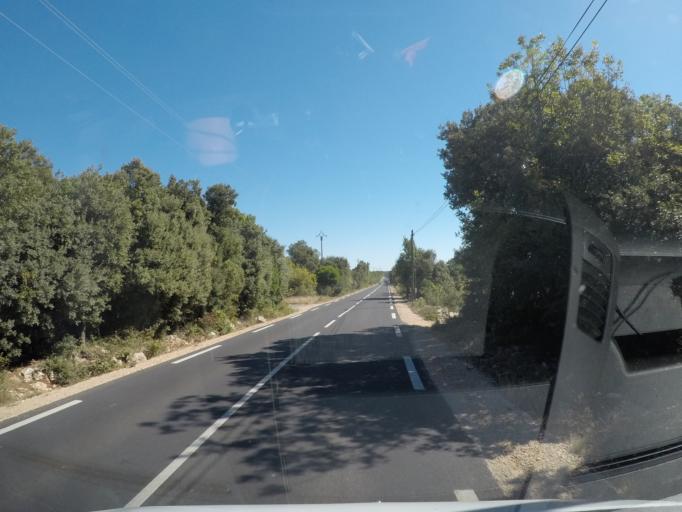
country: FR
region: Languedoc-Roussillon
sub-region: Departement de l'Herault
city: Aniane
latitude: 43.7291
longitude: 3.6365
